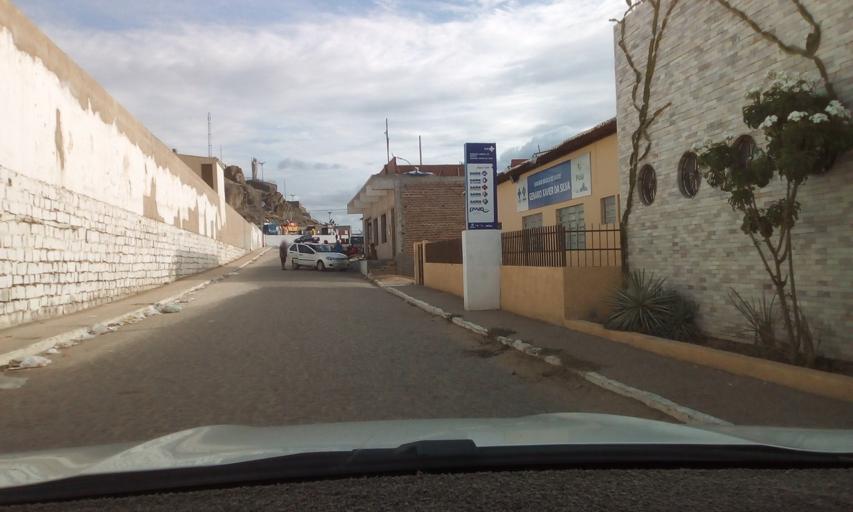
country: BR
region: Paraiba
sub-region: Picui
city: Picui
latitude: -6.5073
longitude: -36.3496
